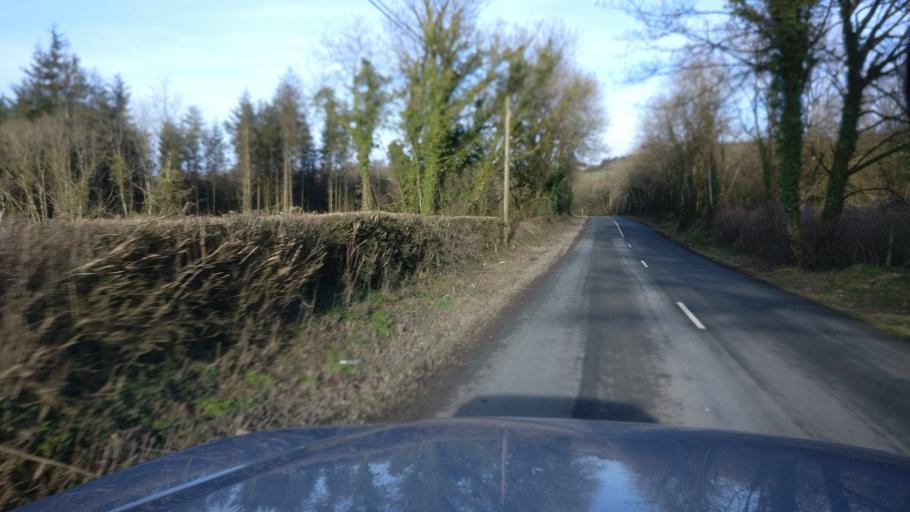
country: IE
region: Leinster
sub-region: Laois
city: Stradbally
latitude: 52.9346
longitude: -7.1971
